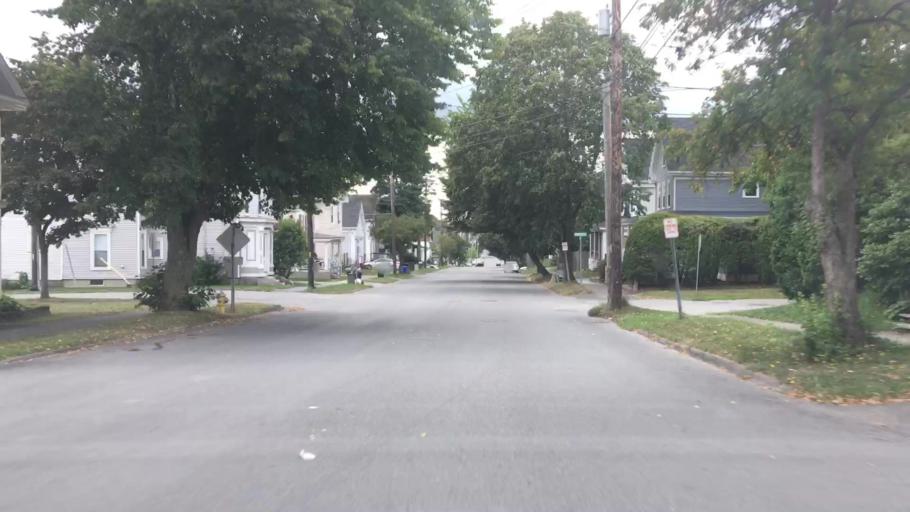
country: US
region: Maine
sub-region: Penobscot County
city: Bangor
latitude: 44.8126
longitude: -68.7729
